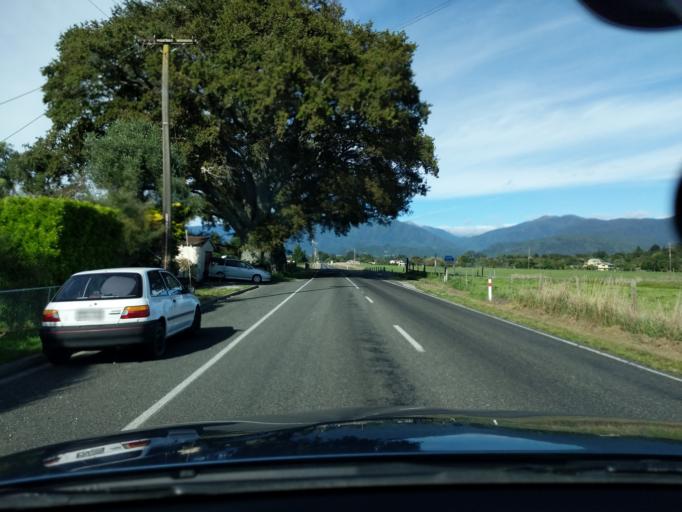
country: NZ
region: Tasman
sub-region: Tasman District
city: Takaka
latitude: -40.8512
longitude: 172.8304
